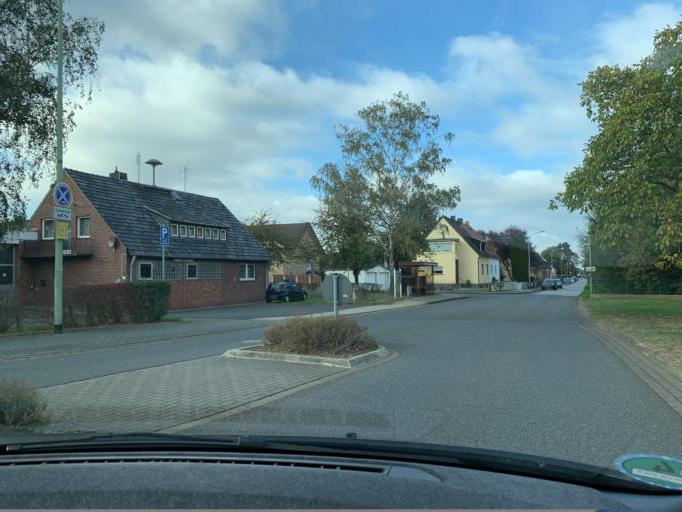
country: DE
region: North Rhine-Westphalia
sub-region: Regierungsbezirk Koln
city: Niederzier
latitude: 50.8504
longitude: 6.4505
